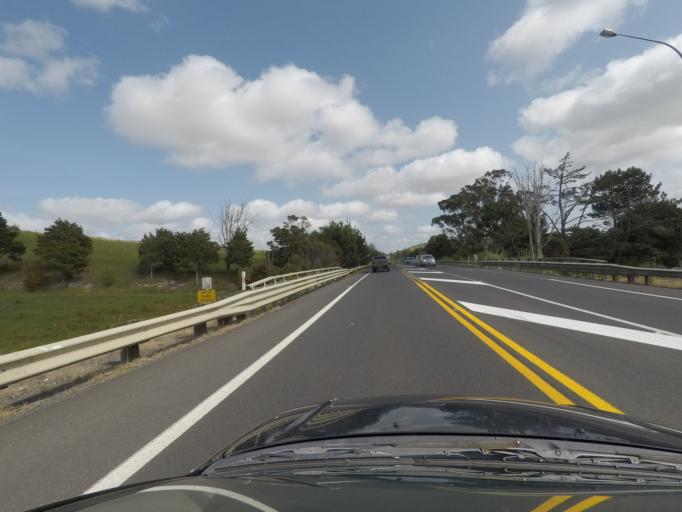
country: NZ
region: Northland
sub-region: Whangarei
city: Whangarei
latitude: -35.8325
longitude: 174.3152
